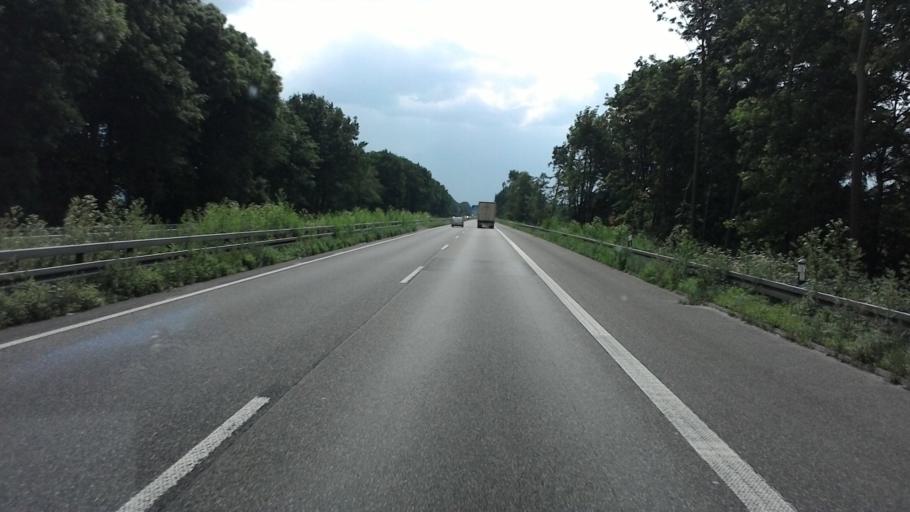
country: DE
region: North Rhine-Westphalia
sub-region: Regierungsbezirk Koln
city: Aachen
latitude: 50.7409
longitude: 6.1400
